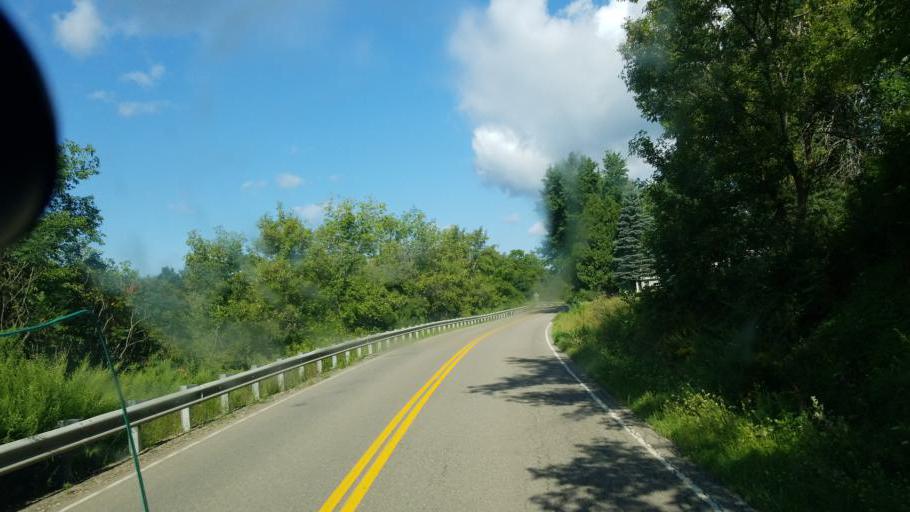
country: US
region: New York
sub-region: Steuben County
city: Canisteo
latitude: 42.2716
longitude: -77.5934
